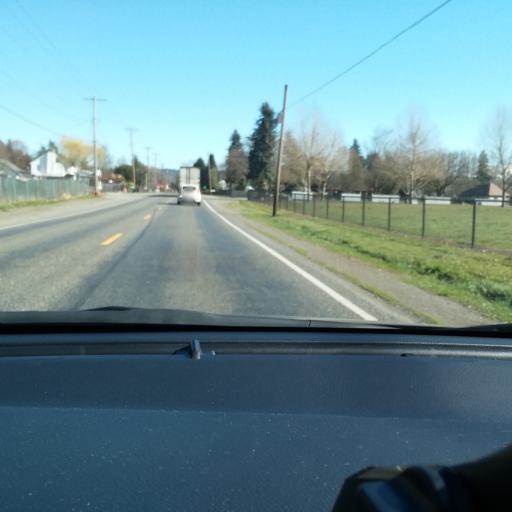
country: US
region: Washington
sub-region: Pierce County
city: North Puyallup
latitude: 47.2052
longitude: -122.2669
